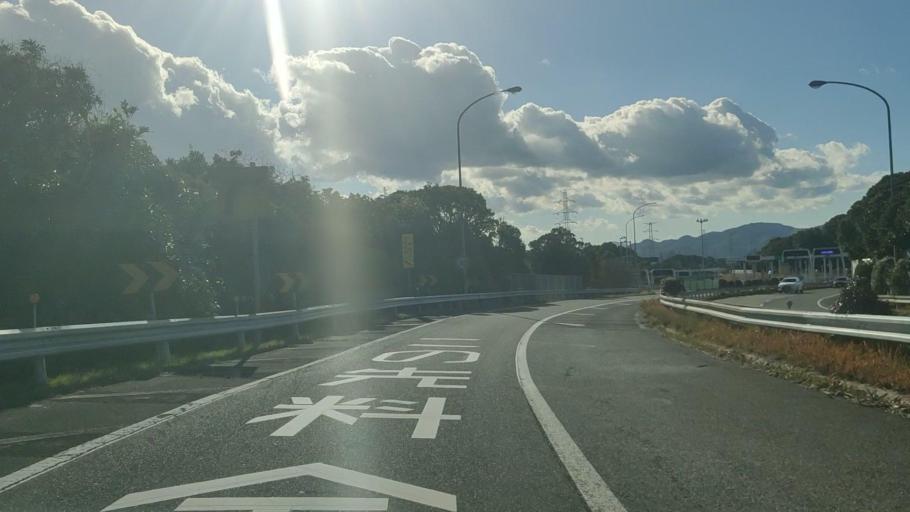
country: JP
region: Fukuoka
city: Nogata
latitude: 33.7830
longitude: 130.7460
